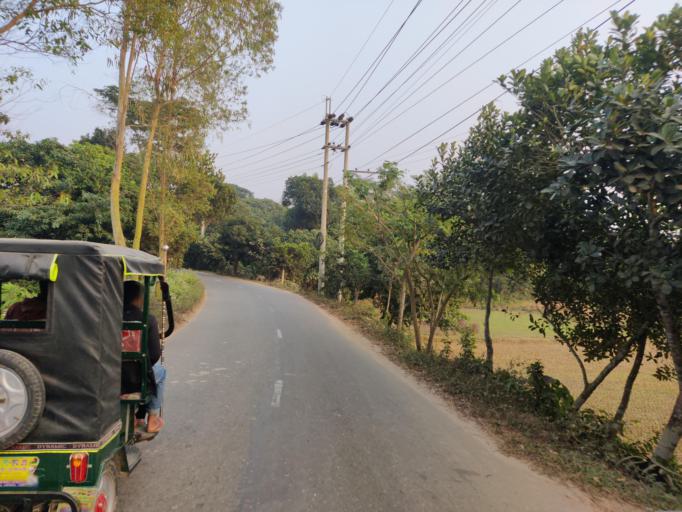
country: BD
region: Dhaka
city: Bajitpur
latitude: 24.1560
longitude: 90.7702
